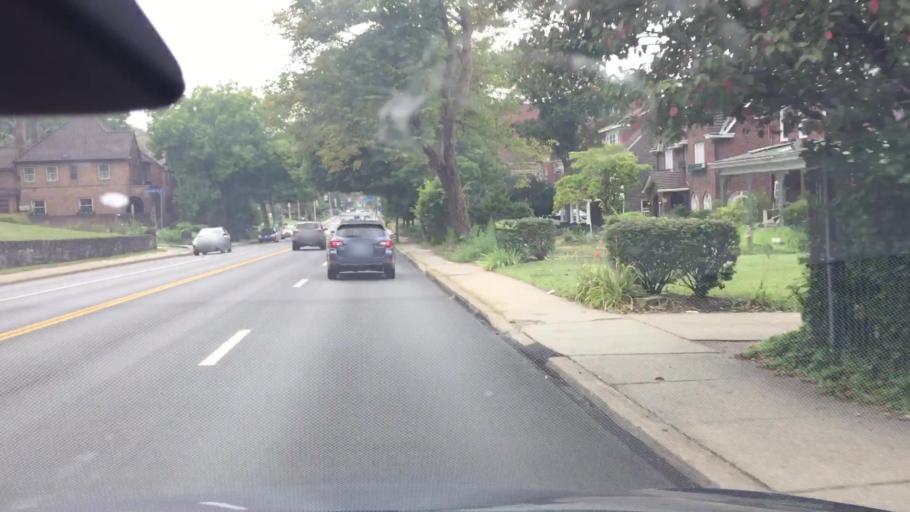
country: US
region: Pennsylvania
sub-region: Allegheny County
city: Bloomfield
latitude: 40.4505
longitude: -79.9277
